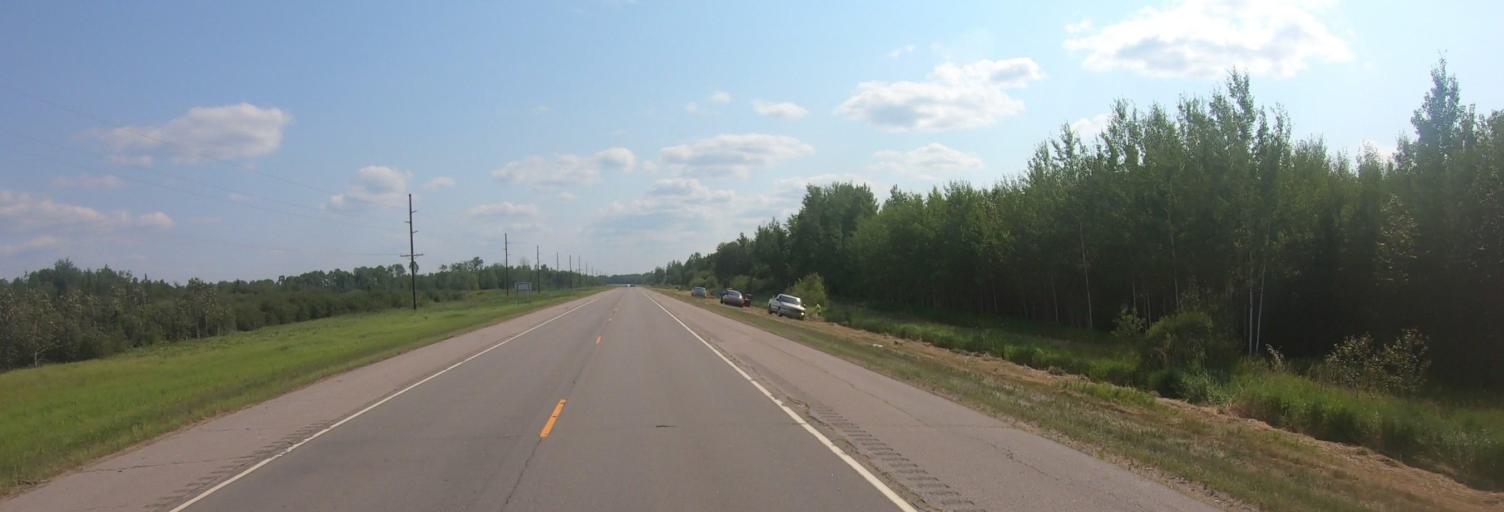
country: US
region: Minnesota
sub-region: Saint Louis County
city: Chisholm
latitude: 47.9442
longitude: -92.8283
